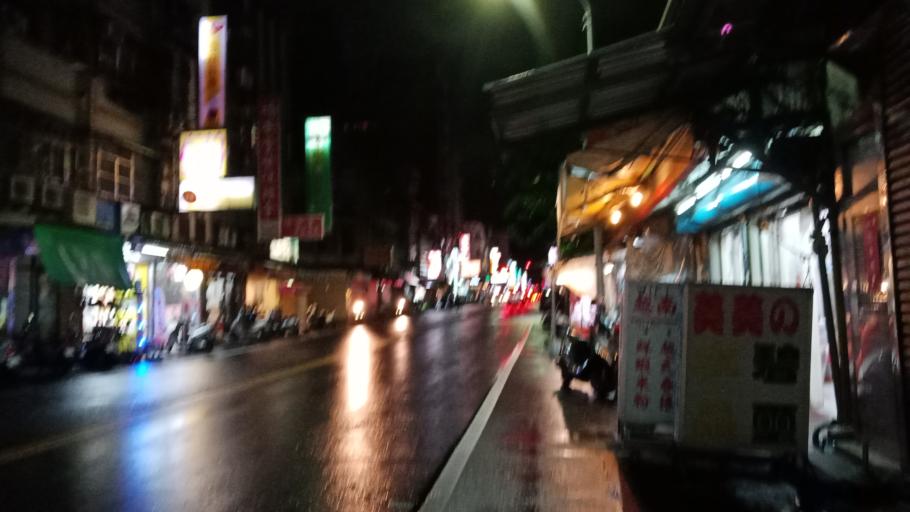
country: TW
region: Taiwan
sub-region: Hsinchu
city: Hsinchu
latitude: 24.7972
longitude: 120.9744
